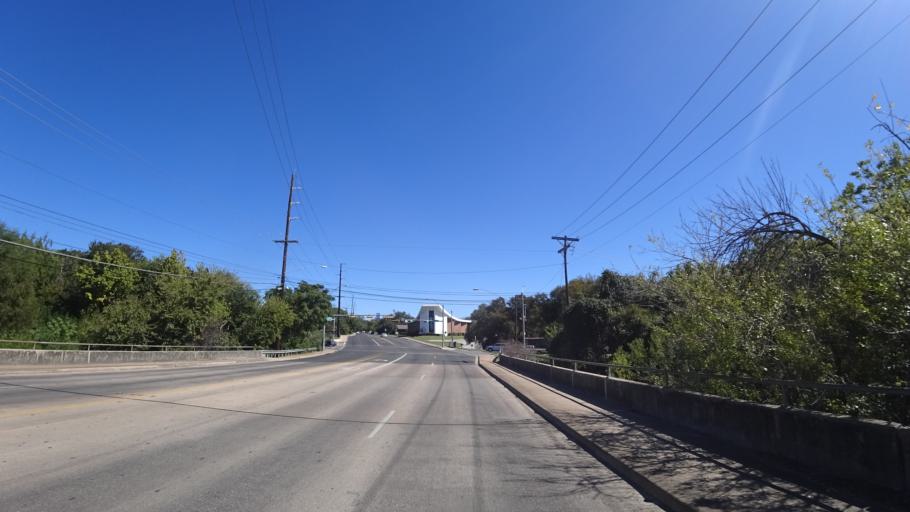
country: US
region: Texas
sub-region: Travis County
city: West Lake Hills
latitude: 30.3345
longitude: -97.7498
